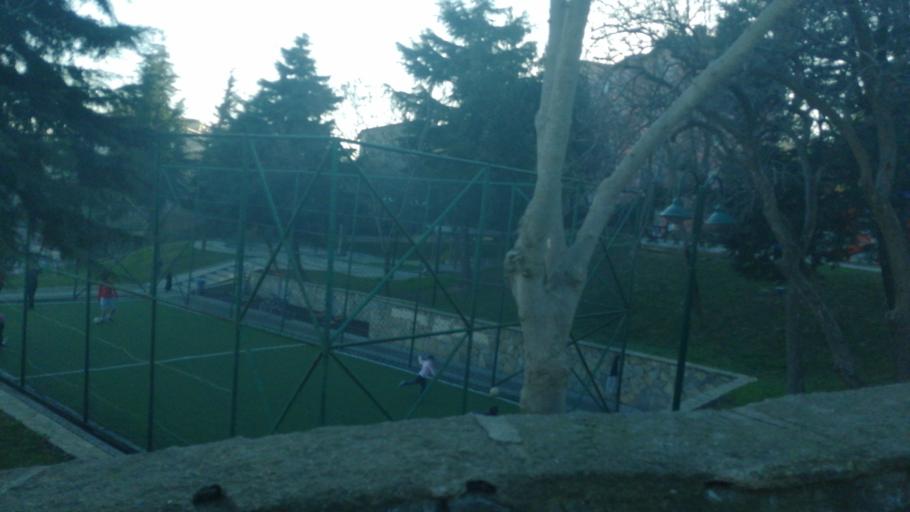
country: TR
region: Istanbul
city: UEskuedar
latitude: 41.0558
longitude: 29.0672
